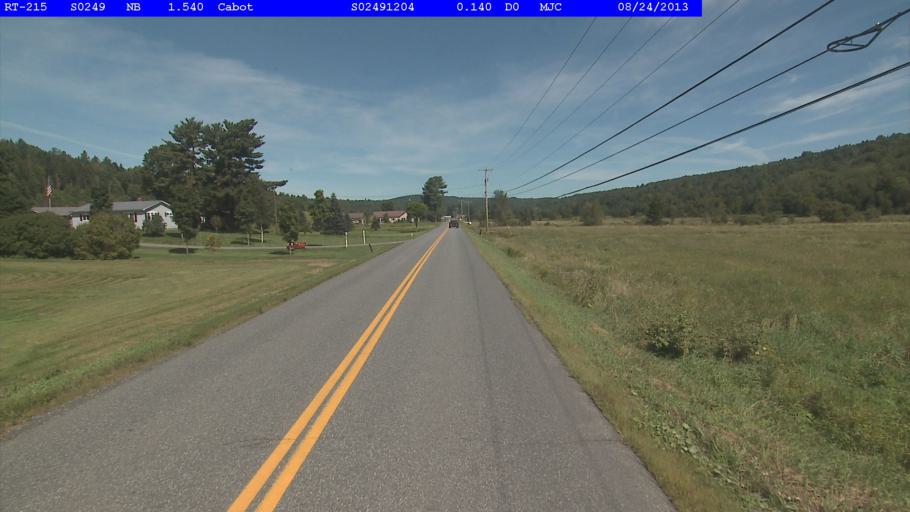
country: US
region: Vermont
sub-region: Caledonia County
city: Hardwick
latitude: 44.3696
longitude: -72.3368
